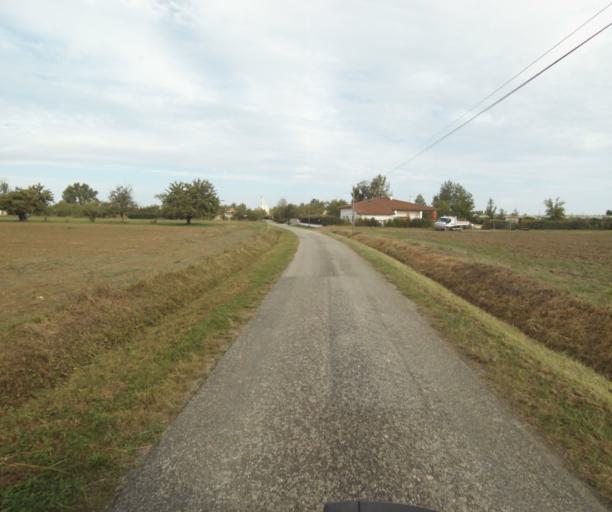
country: FR
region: Midi-Pyrenees
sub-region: Departement du Tarn-et-Garonne
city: Montech
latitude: 43.9430
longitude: 1.2215
